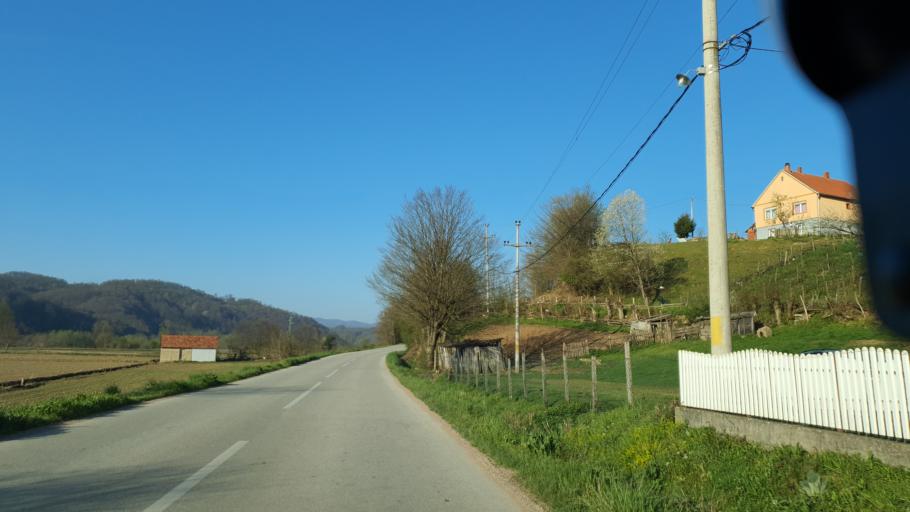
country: RS
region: Central Serbia
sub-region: Kolubarski Okrug
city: Osecina
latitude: 44.3857
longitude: 19.5622
